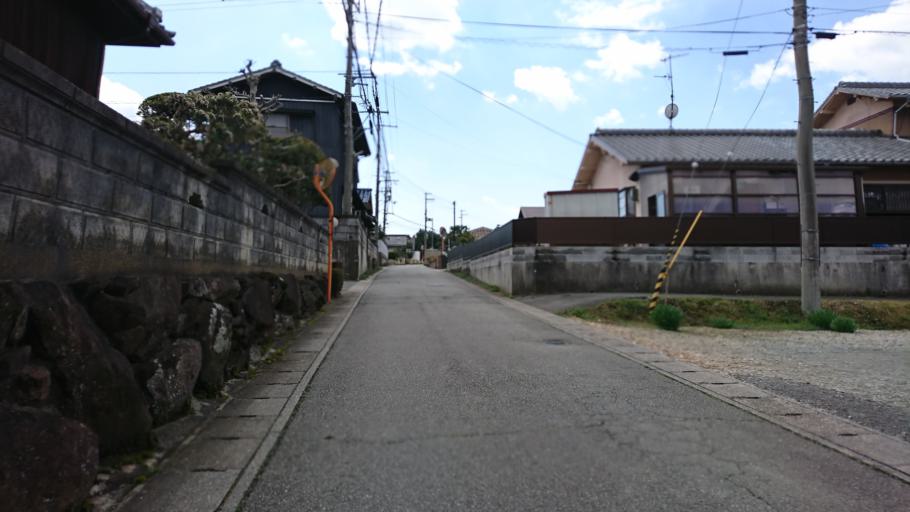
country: JP
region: Hyogo
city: Miki
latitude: 34.7619
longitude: 134.9548
